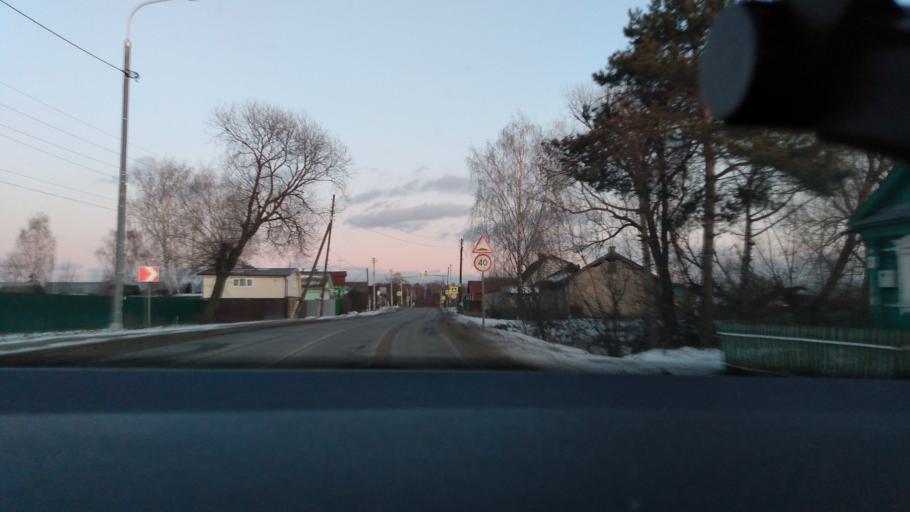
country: RU
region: Moskovskaya
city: Krasnaya Poyma
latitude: 55.1114
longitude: 39.0296
